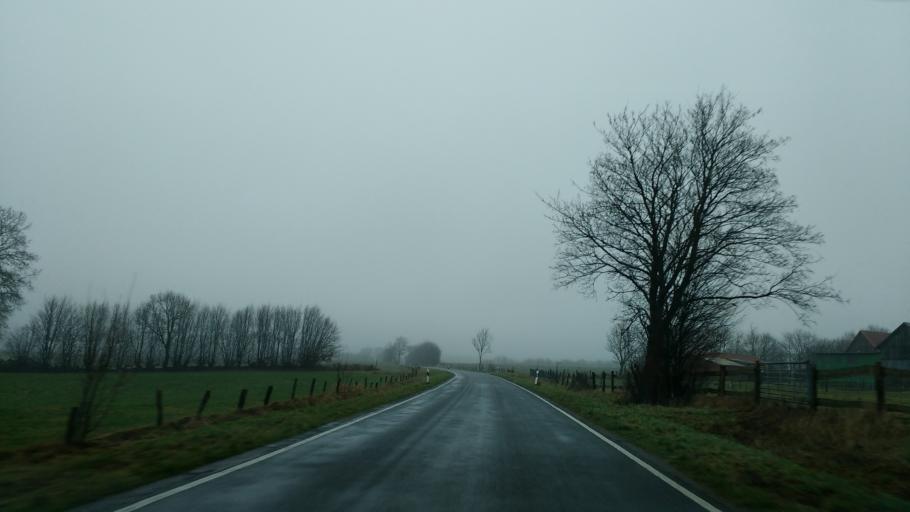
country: DE
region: Schleswig-Holstein
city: Nindorf
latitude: 54.1355
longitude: 9.6924
